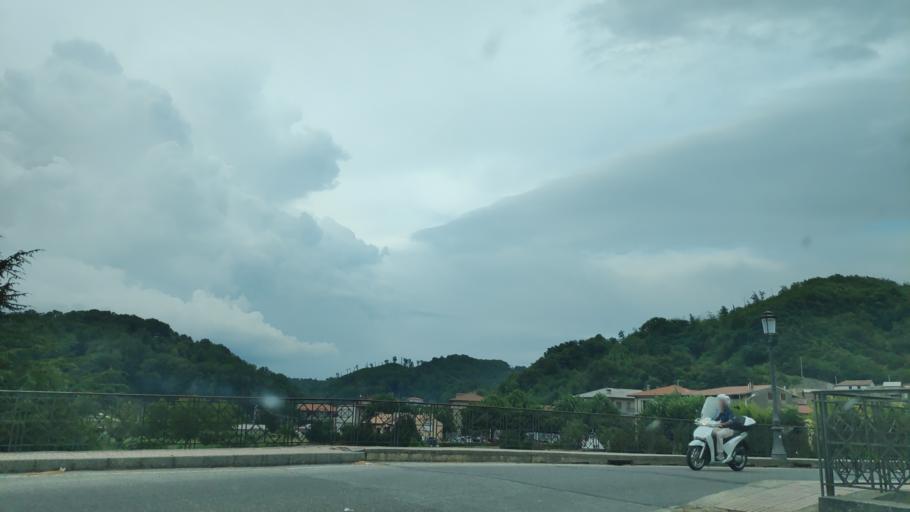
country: IT
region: Calabria
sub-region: Provincia di Catanzaro
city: Cardinale
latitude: 38.6443
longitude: 16.3859
